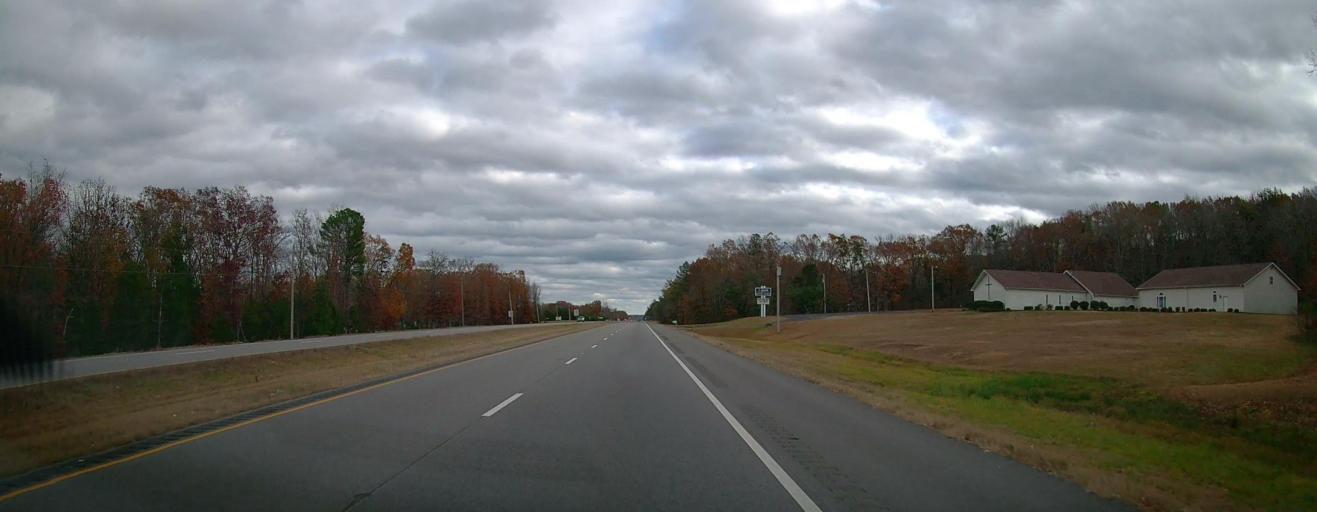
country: US
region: Alabama
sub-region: Colbert County
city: Muscle Shoals
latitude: 34.6671
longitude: -87.5554
